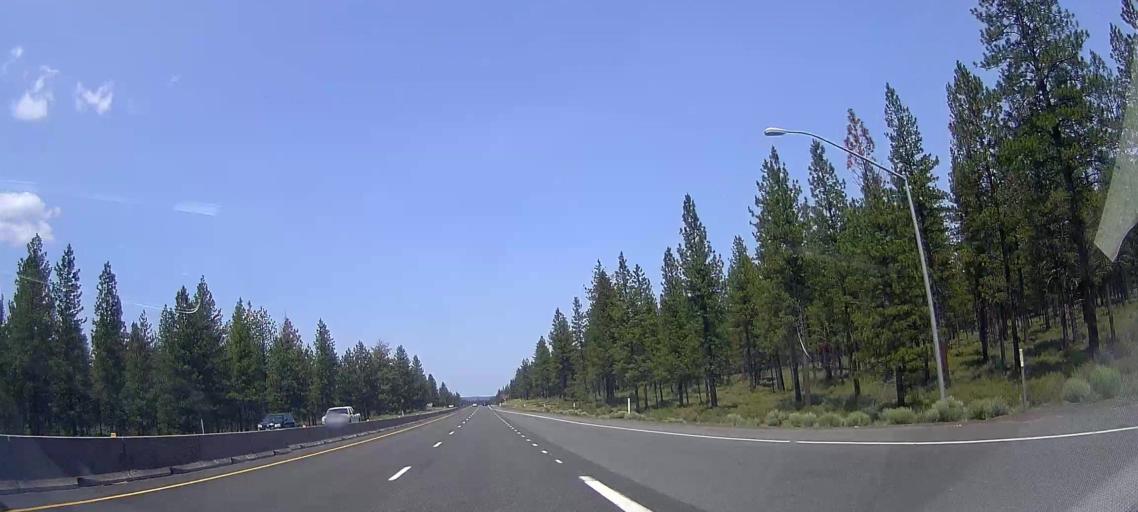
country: US
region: Oregon
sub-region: Deschutes County
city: Deschutes River Woods
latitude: 43.9603
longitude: -121.3479
